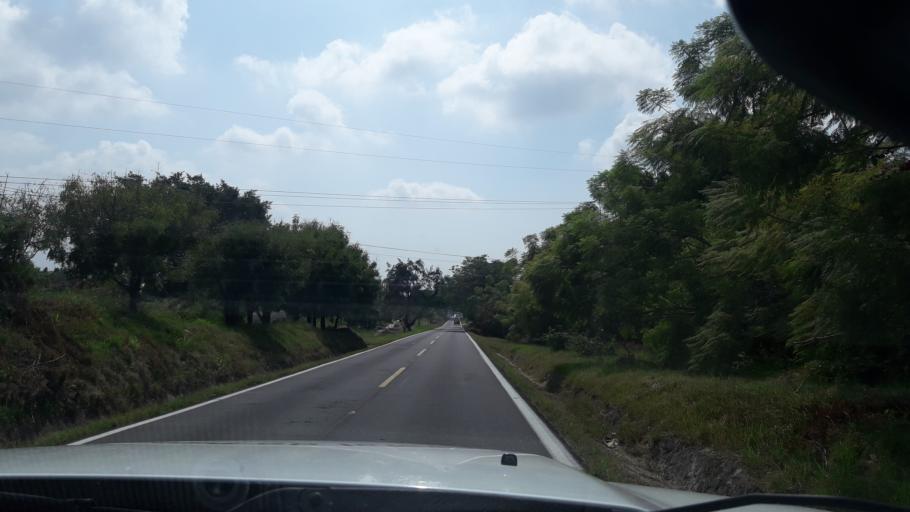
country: MX
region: Colima
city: Suchitlan
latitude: 19.3884
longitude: -103.7088
